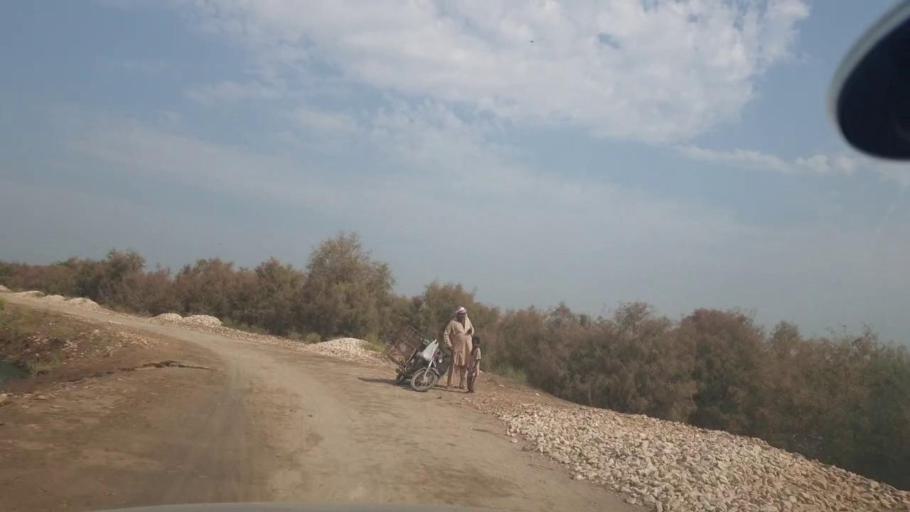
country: PK
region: Balochistan
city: Mehrabpur
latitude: 28.0936
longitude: 68.0950
